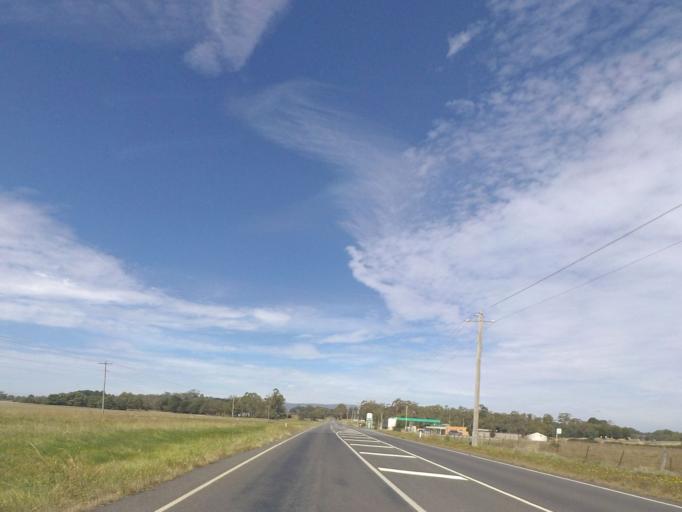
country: AU
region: Victoria
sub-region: Hume
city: Sunbury
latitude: -37.2899
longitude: 144.5045
